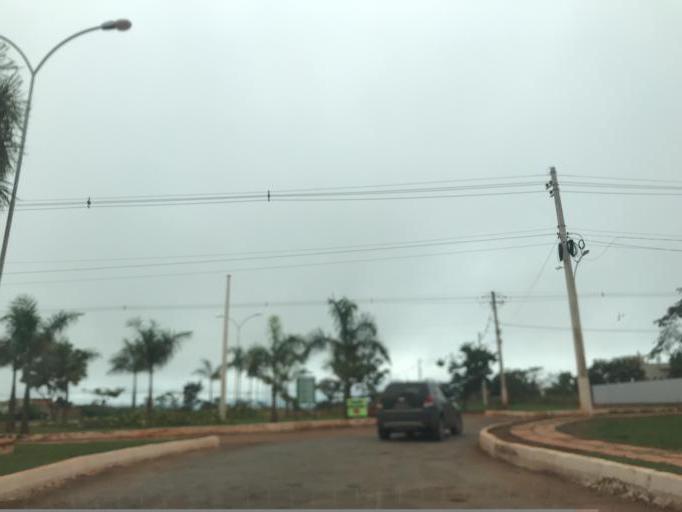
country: BR
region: Federal District
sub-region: Brasilia
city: Brasilia
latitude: -15.8246
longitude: -47.7931
